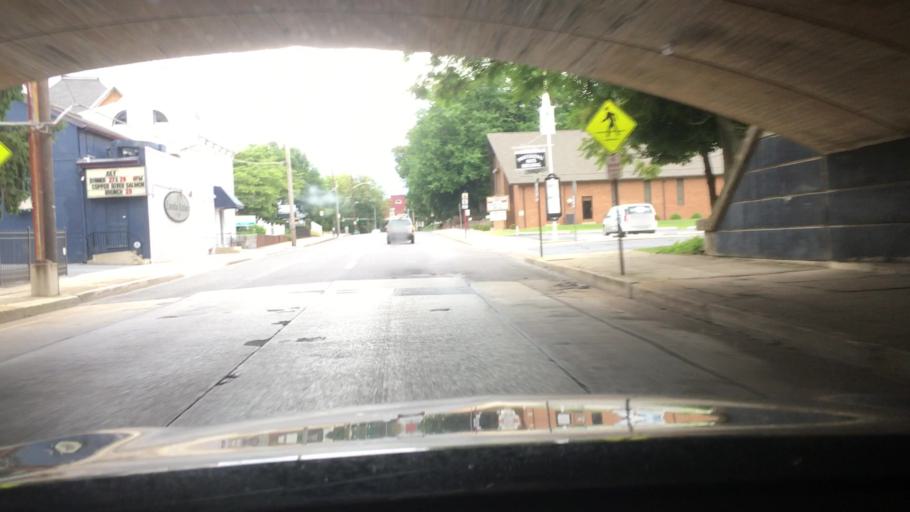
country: US
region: Pennsylvania
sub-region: Franklin County
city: Chambersburg
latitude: 39.9361
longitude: -77.6550
